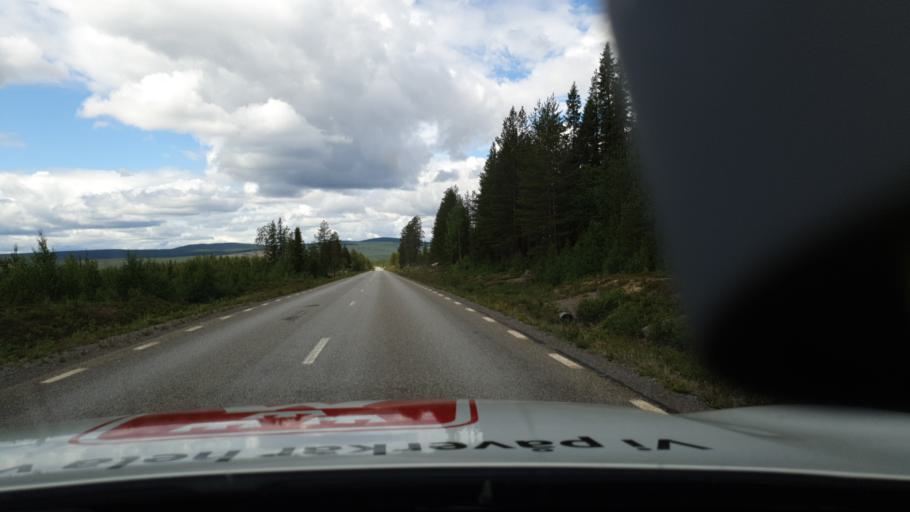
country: SE
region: Norrbotten
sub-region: Arvidsjaurs Kommun
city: Arvidsjaur
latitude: 65.9610
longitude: 19.5716
